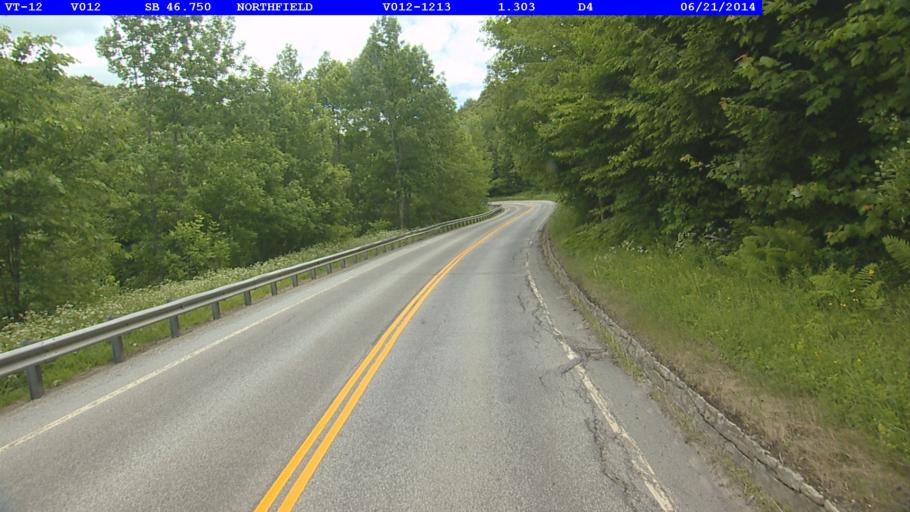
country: US
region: Vermont
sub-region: Washington County
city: Northfield
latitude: 44.1093
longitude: -72.6490
